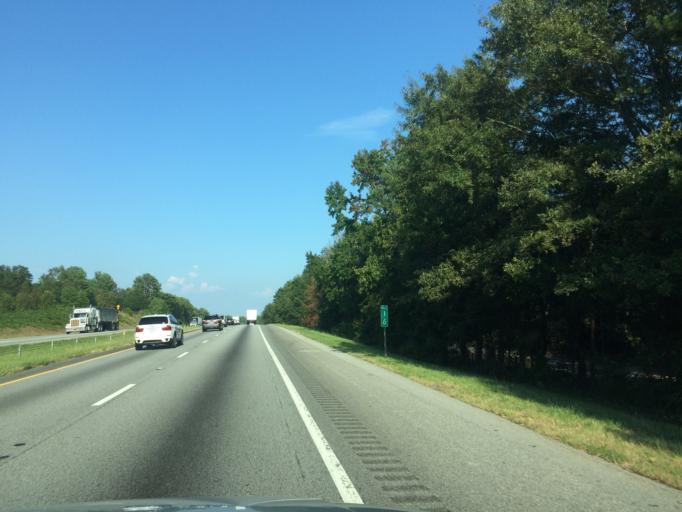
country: US
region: South Carolina
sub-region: Anderson County
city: Centerville
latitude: 34.5593
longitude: -82.7694
